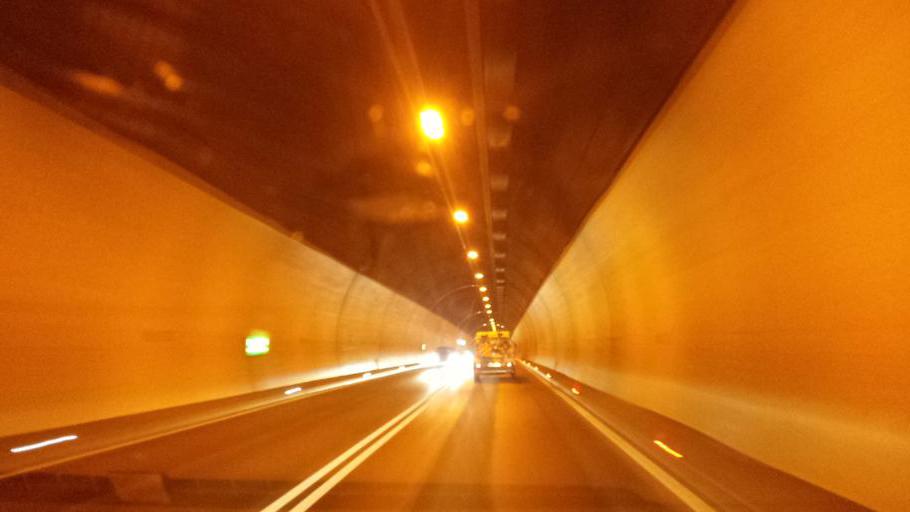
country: AT
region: Upper Austria
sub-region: Politischer Bezirk Gmunden
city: Bad Ischl
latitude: 47.7190
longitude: 13.6147
